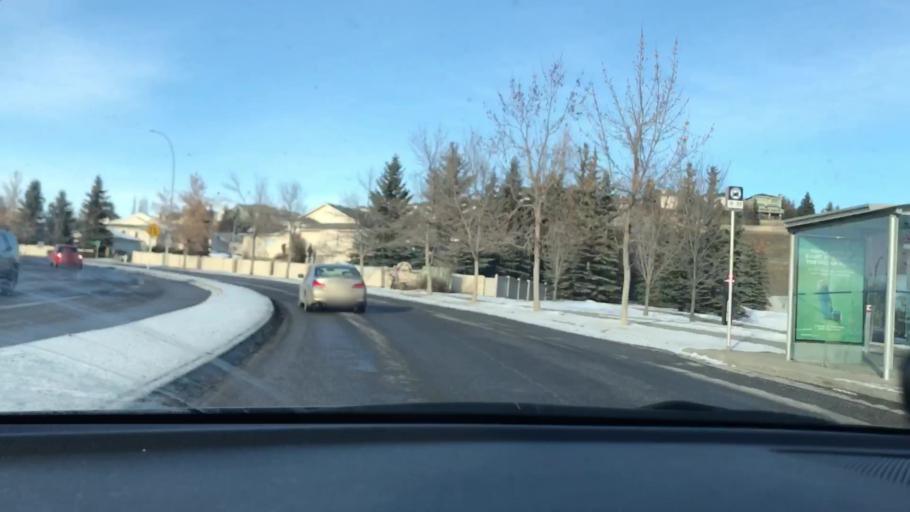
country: CA
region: Alberta
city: Calgary
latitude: 51.0183
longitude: -114.1760
